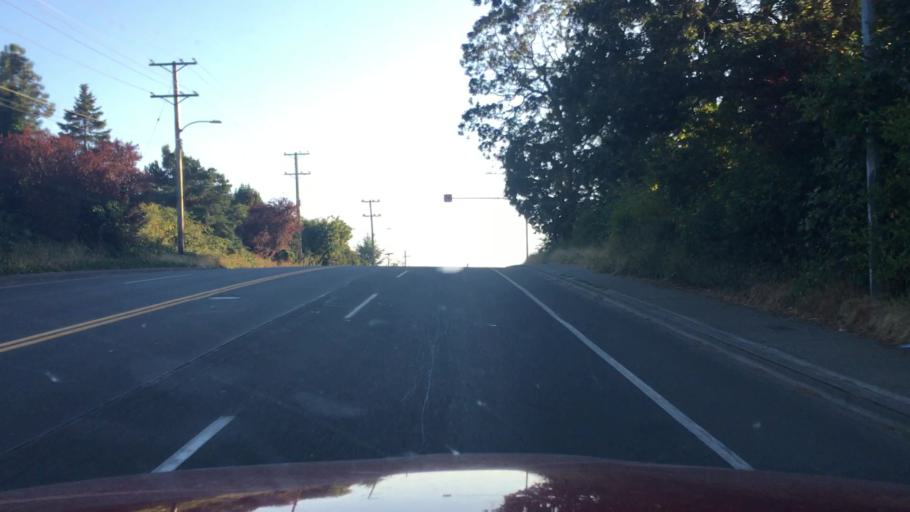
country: CA
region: British Columbia
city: Victoria
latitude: 48.4713
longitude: -123.3557
